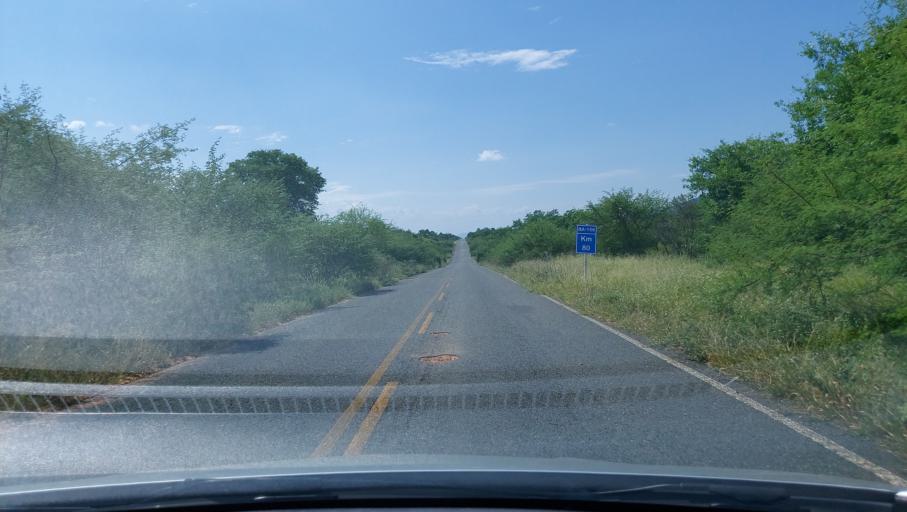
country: BR
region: Bahia
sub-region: Oliveira Dos Brejinhos
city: Beira Rio
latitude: -12.1489
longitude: -42.5544
